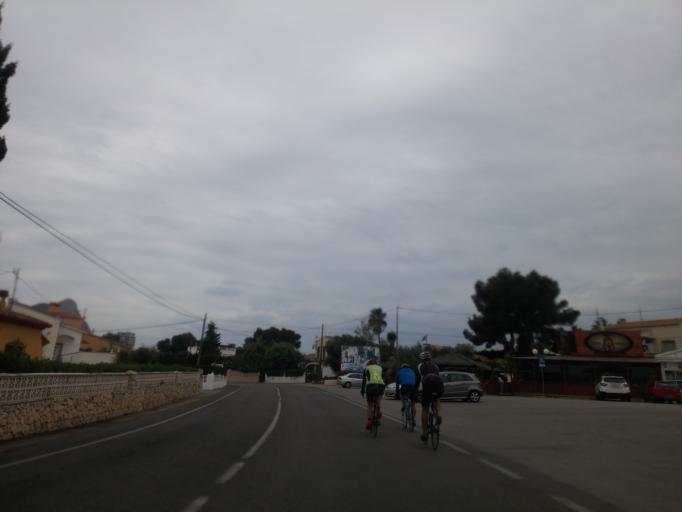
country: ES
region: Valencia
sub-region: Provincia de Alicante
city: Calp
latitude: 38.6577
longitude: 0.0776
